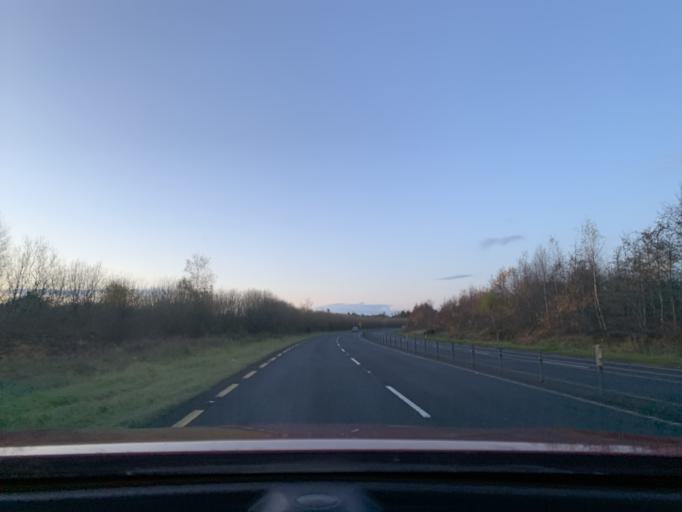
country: IE
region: Connaught
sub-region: County Leitrim
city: Carrick-on-Shannon
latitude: 53.8733
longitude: -7.9276
